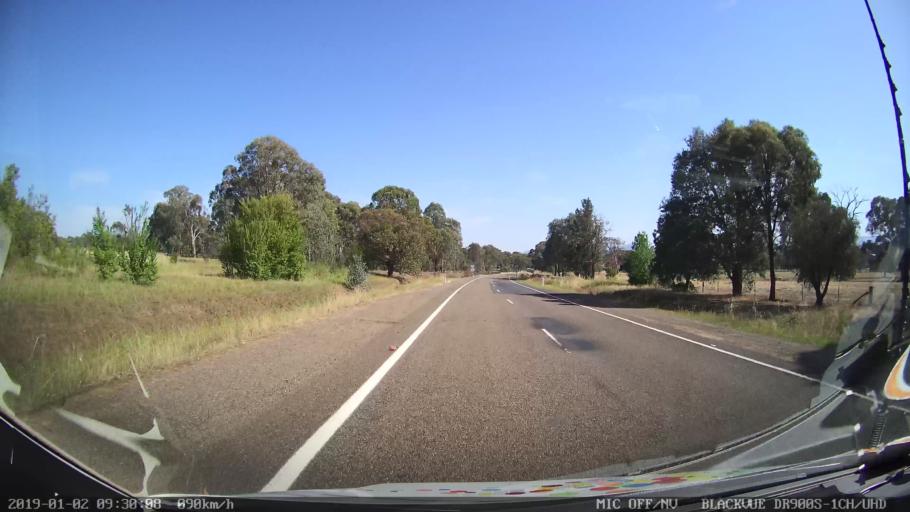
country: AU
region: New South Wales
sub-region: Tumut Shire
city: Tumut
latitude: -35.3303
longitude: 148.2377
